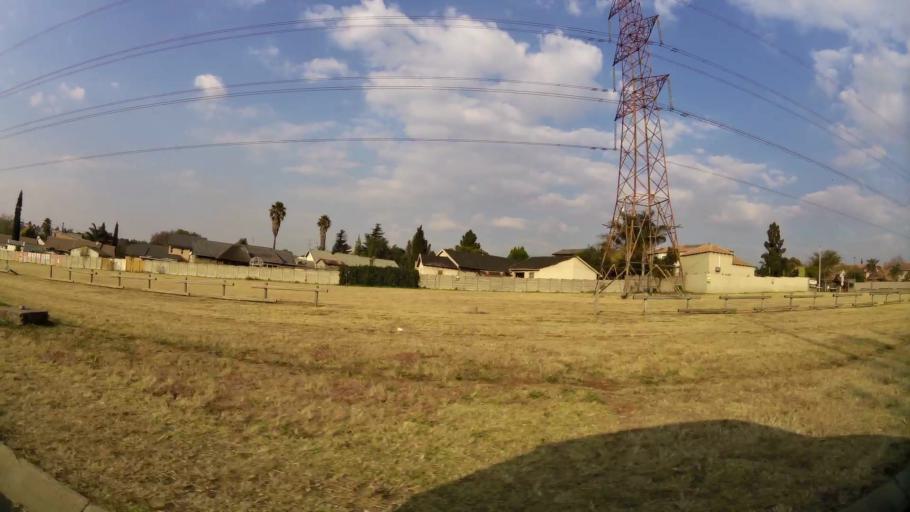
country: ZA
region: Gauteng
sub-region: City of Johannesburg Metropolitan Municipality
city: Modderfontein
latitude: -26.1323
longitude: 28.1836
